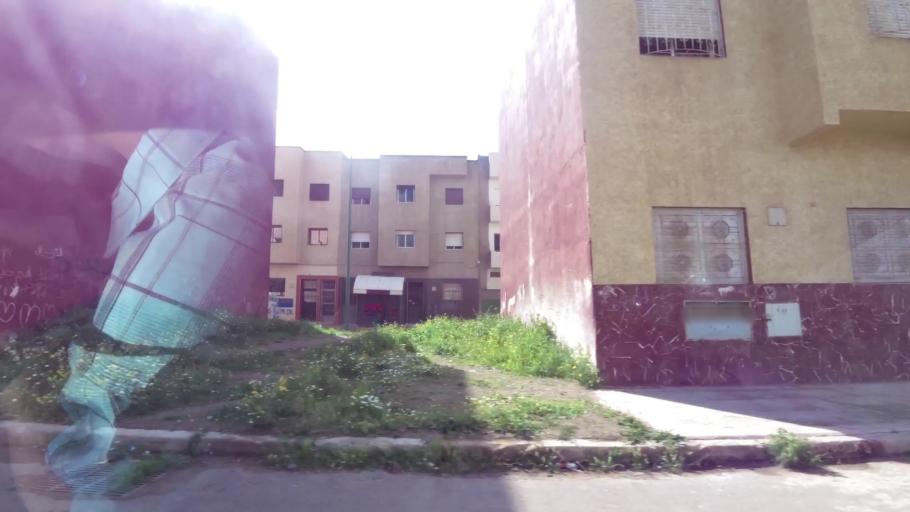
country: MA
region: Chaouia-Ouardigha
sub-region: Settat Province
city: Berrechid
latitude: 33.2611
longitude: -7.5635
